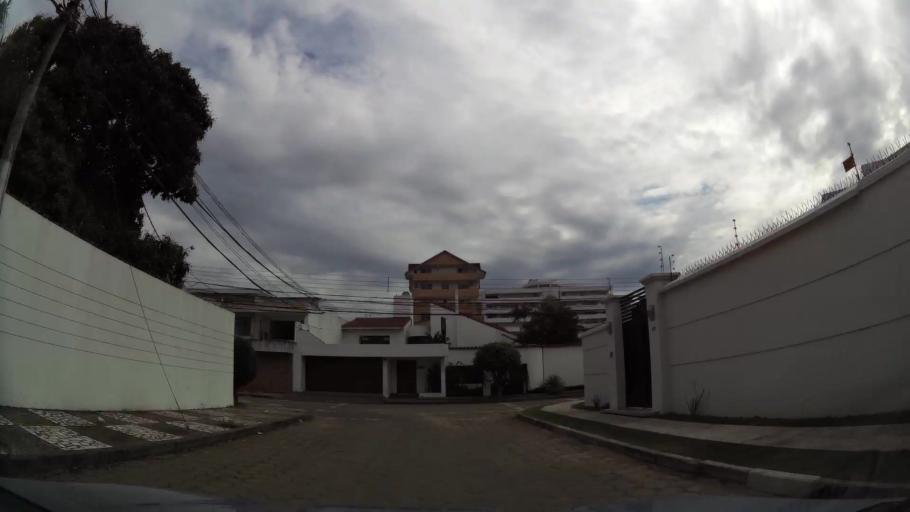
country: BO
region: Santa Cruz
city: Santa Cruz de la Sierra
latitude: -17.7976
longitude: -63.1951
